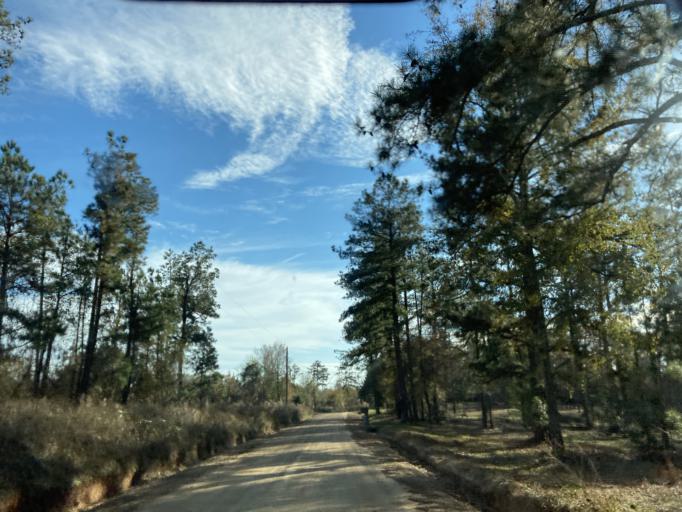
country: US
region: Georgia
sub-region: Jones County
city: Gray
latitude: 32.8894
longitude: -83.4881
